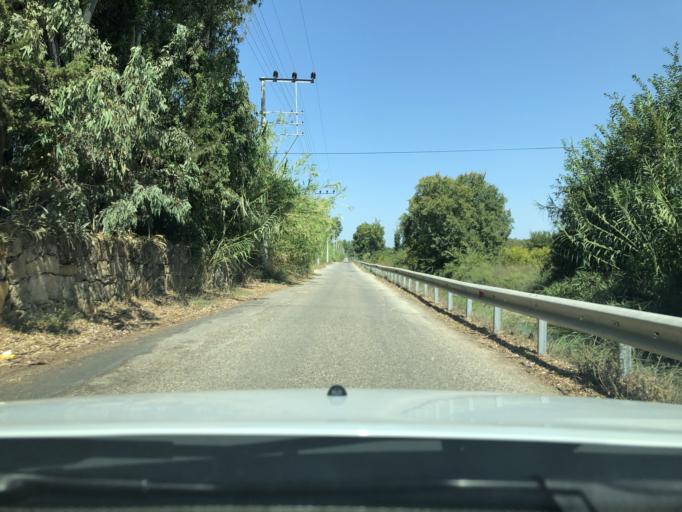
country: TR
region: Antalya
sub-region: Manavgat
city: Manavgat
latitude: 36.8034
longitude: 31.4681
